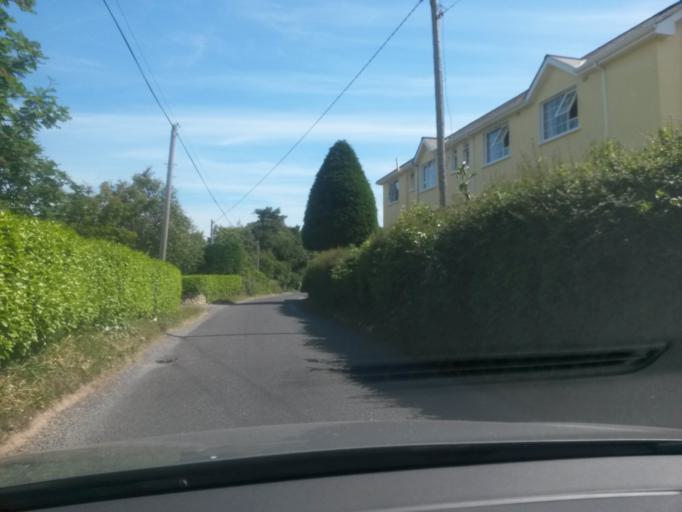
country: IE
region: Leinster
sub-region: Wicklow
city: Enniskerry
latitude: 53.1666
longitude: -6.1885
